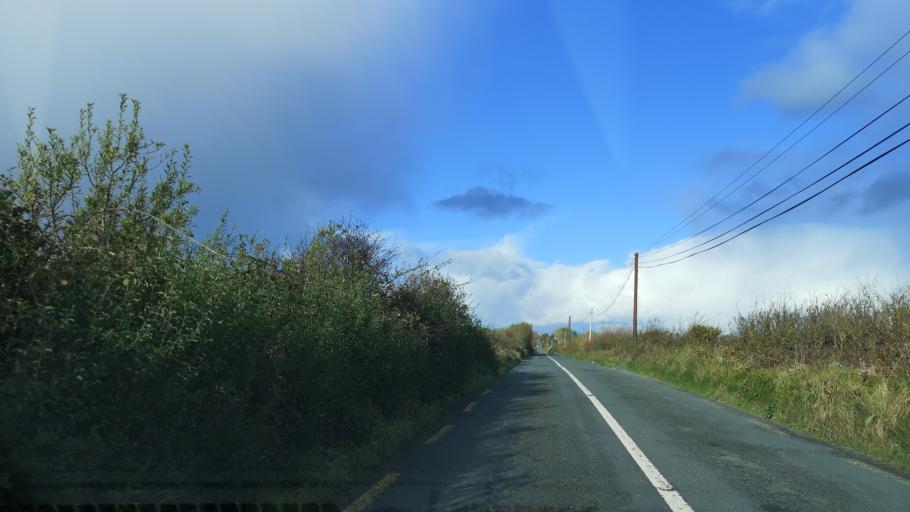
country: IE
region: Connaught
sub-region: Maigh Eo
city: Castlebar
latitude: 53.7636
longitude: -9.3765
